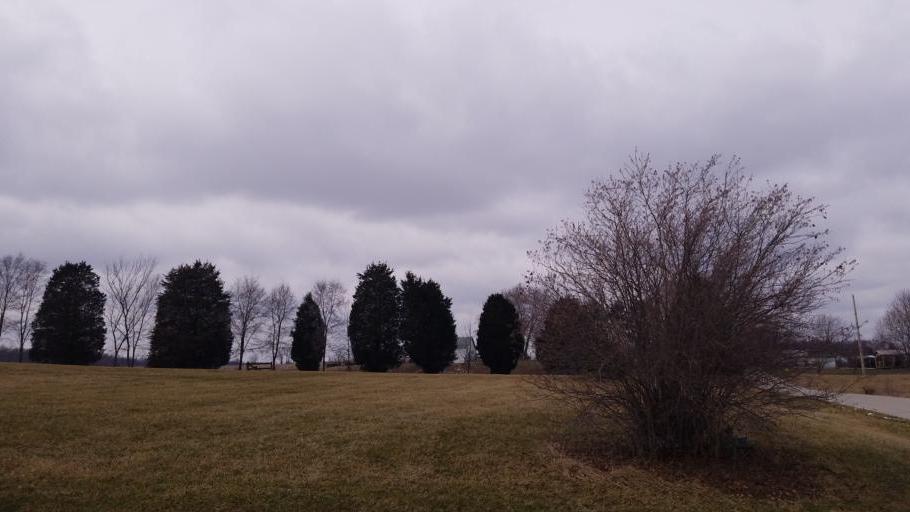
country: US
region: Ohio
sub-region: Crawford County
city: Galion
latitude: 40.6654
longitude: -82.7088
